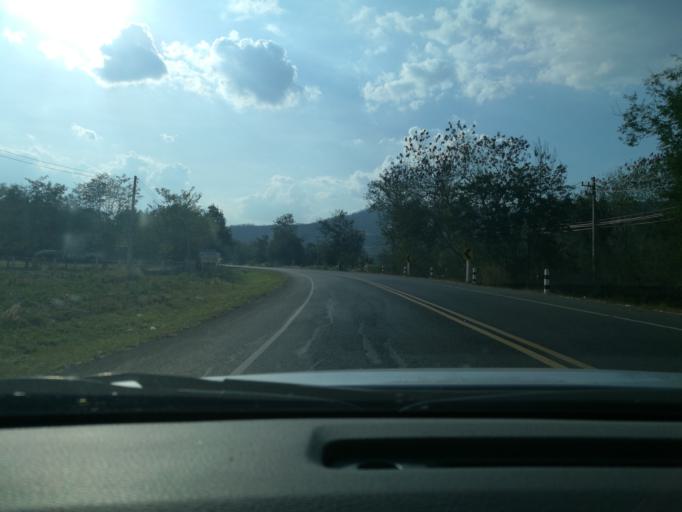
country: TH
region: Phetchabun
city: Phetchabun
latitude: 16.5485
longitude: 101.1262
